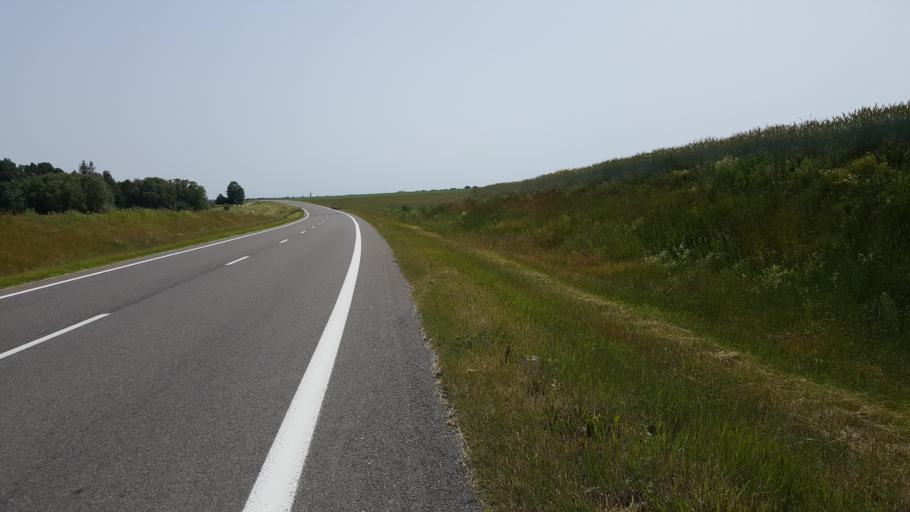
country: BY
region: Brest
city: Kamyanyets
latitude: 52.4406
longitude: 23.8314
